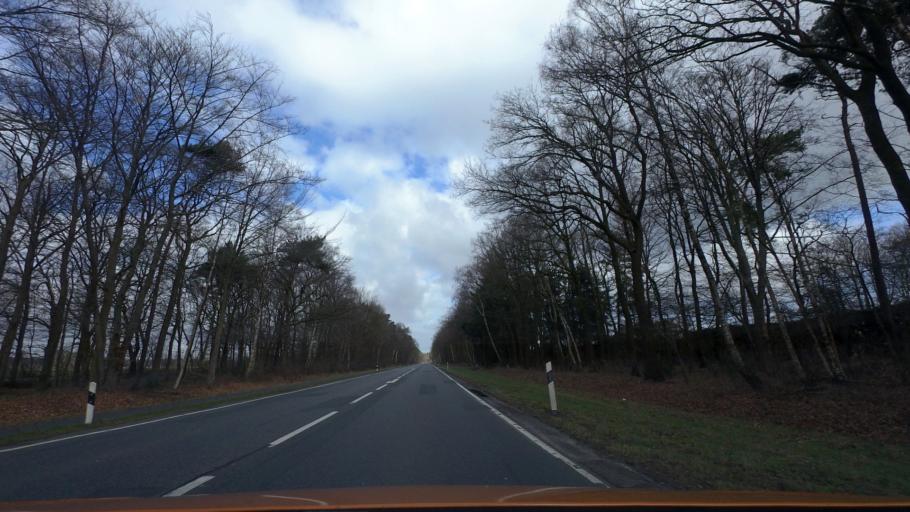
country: DE
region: Lower Saxony
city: Molbergen
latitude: 52.9278
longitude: 7.9500
